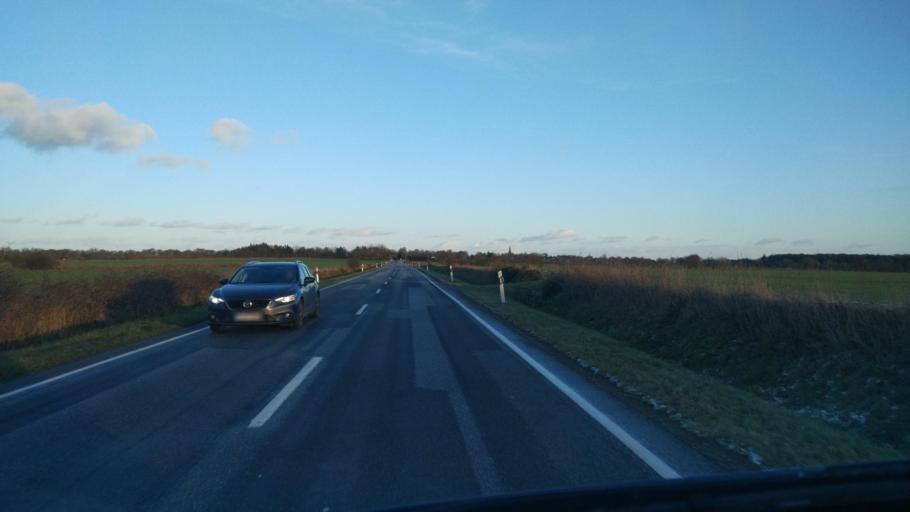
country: DE
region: Schleswig-Holstein
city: Wittbek
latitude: 54.4623
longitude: 9.2070
